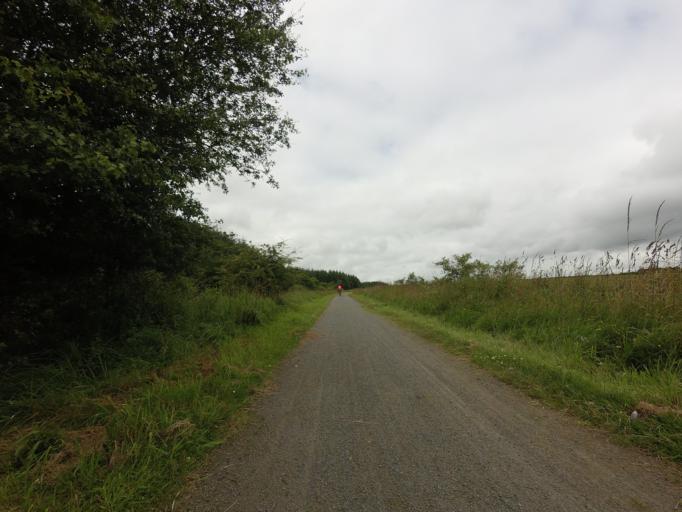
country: GB
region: Scotland
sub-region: Aberdeenshire
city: Mintlaw
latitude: 57.4949
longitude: -2.1381
